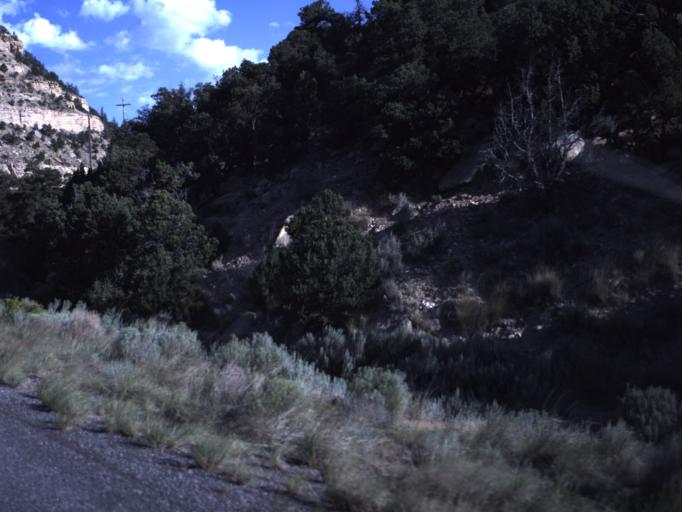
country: US
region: Utah
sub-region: Emery County
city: Huntington
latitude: 39.3957
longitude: -111.1075
